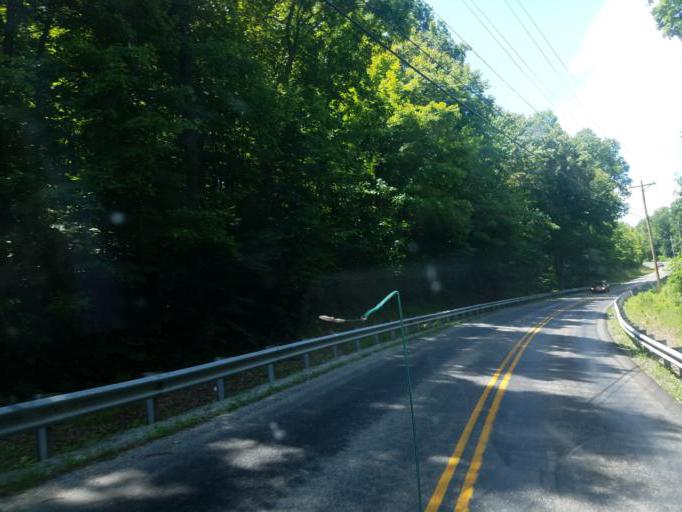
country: US
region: Kentucky
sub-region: Grayson County
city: Leitchfield
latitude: 37.5026
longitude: -86.4728
